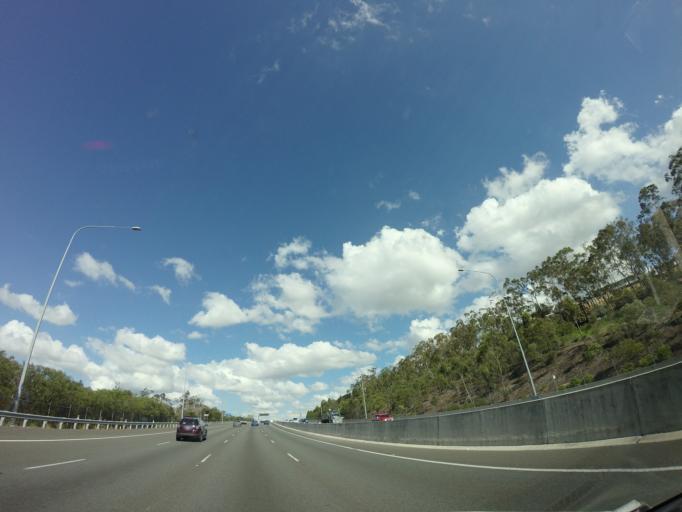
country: AU
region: Queensland
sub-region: Ipswich
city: Redbank
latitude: -27.6010
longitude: 152.8817
